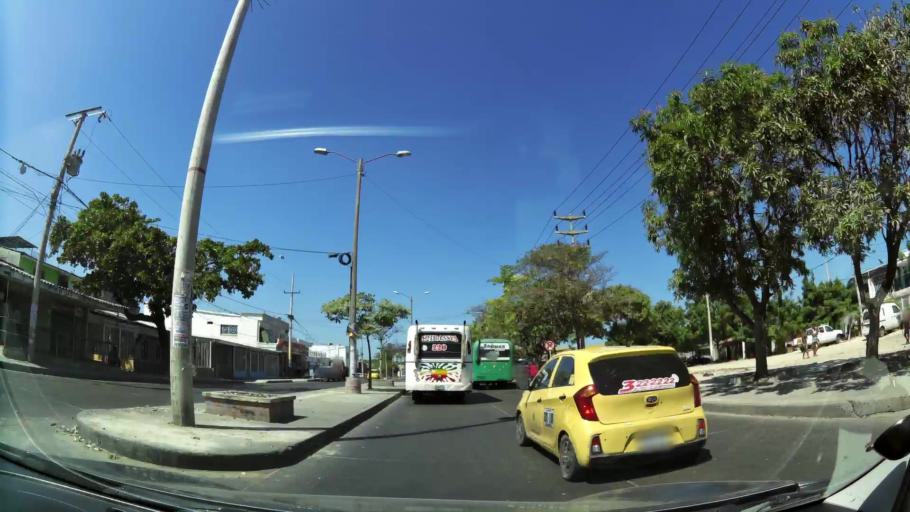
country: CO
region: Atlantico
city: Barranquilla
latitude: 10.9561
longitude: -74.7742
